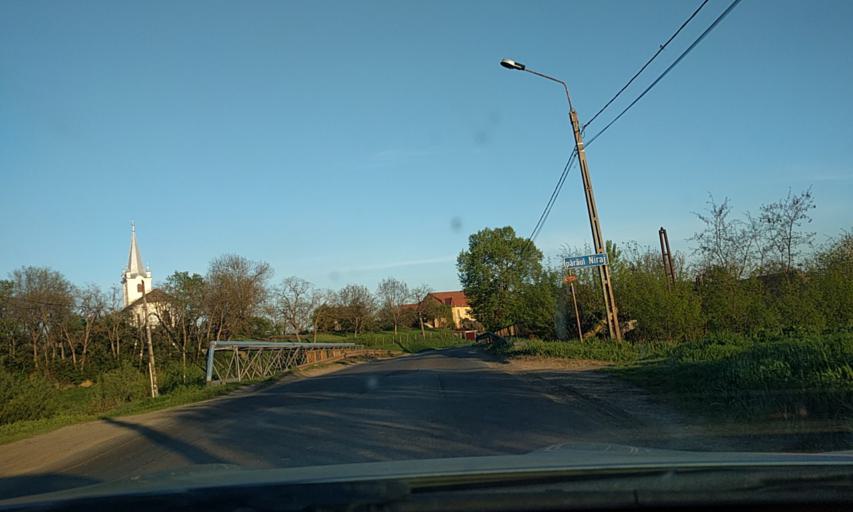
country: RO
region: Mures
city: Gheorghe Doja
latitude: 46.4715
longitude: 24.4831
